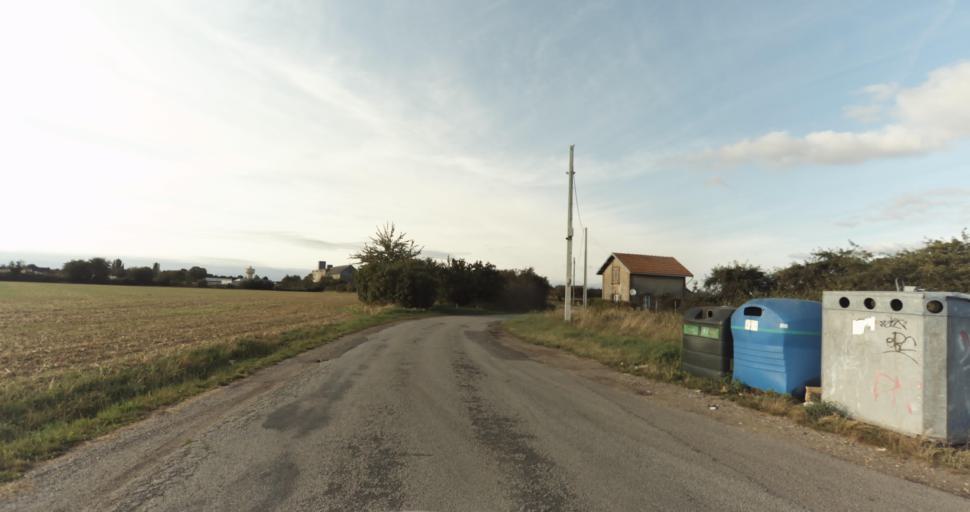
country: FR
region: Haute-Normandie
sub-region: Departement de l'Eure
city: Marcilly-sur-Eure
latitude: 48.8981
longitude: 1.2755
